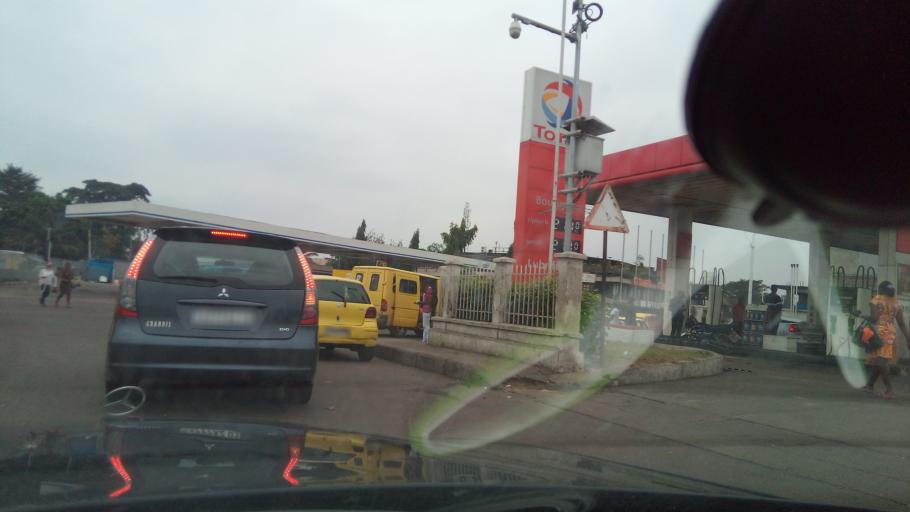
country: CD
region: Kinshasa
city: Kinshasa
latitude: -4.3339
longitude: 15.2580
